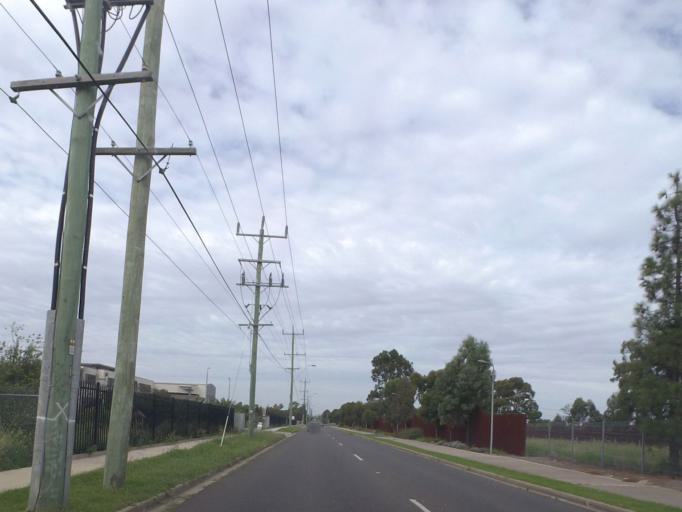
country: AU
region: Victoria
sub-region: Brimbank
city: Sunshine West
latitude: -37.7836
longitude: 144.8103
